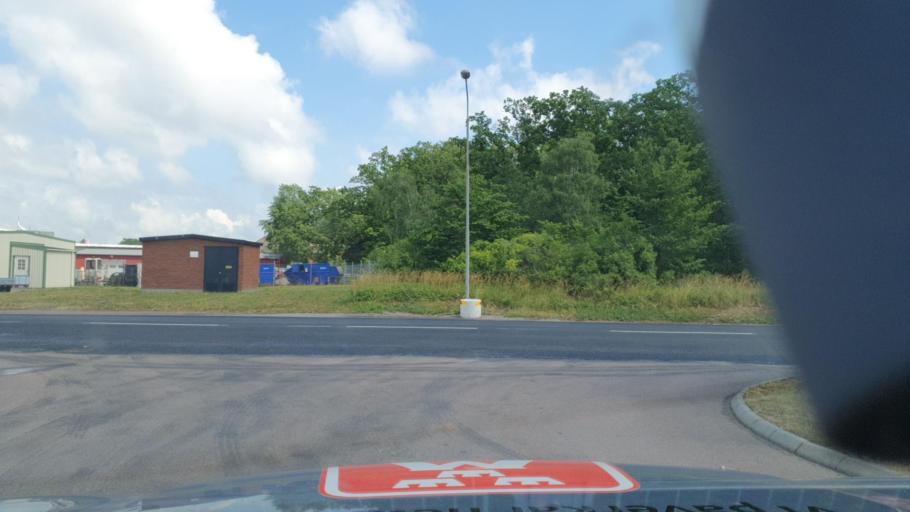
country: SE
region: Kalmar
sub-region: Kalmar Kommun
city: Lindsdal
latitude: 56.6940
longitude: 16.3195
